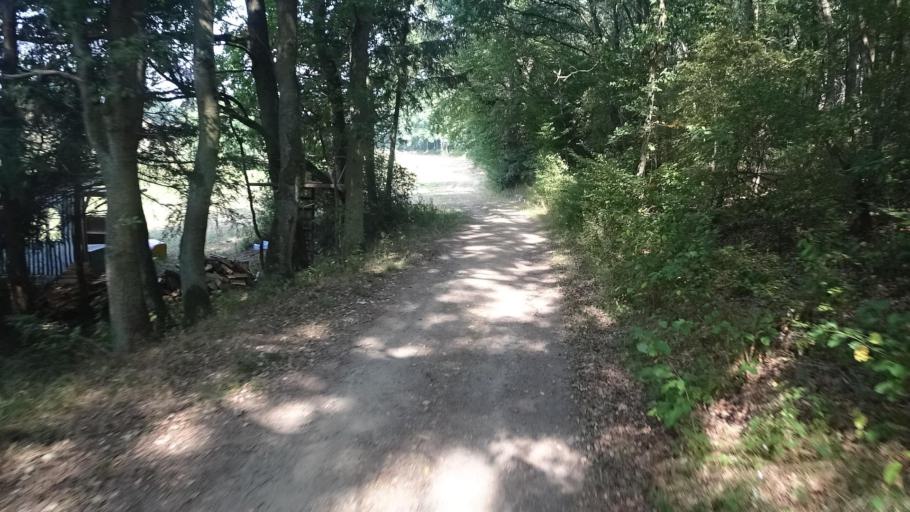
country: DE
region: Rheinland-Pfalz
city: Mutterschied
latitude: 49.9893
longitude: 7.5583
